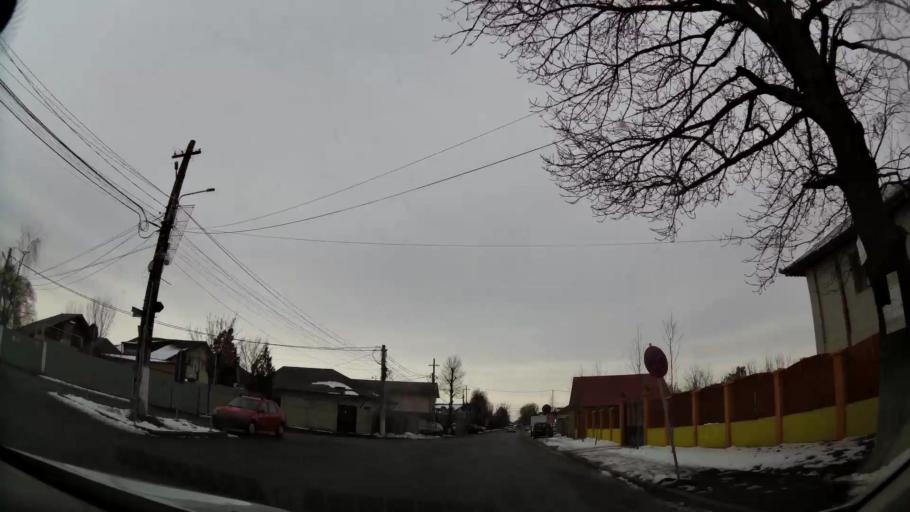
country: RO
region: Ilfov
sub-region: Comuna Pantelimon
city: Pantelimon
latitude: 44.4650
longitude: 26.2121
